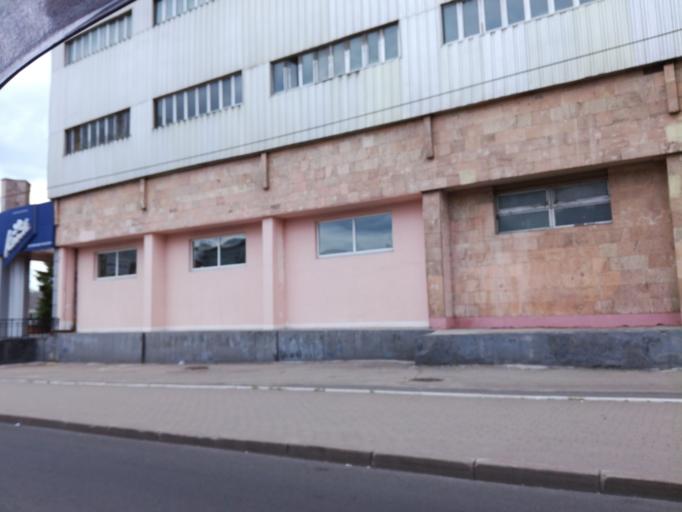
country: RU
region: Kursk
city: Kursk
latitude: 51.7366
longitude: 36.1900
